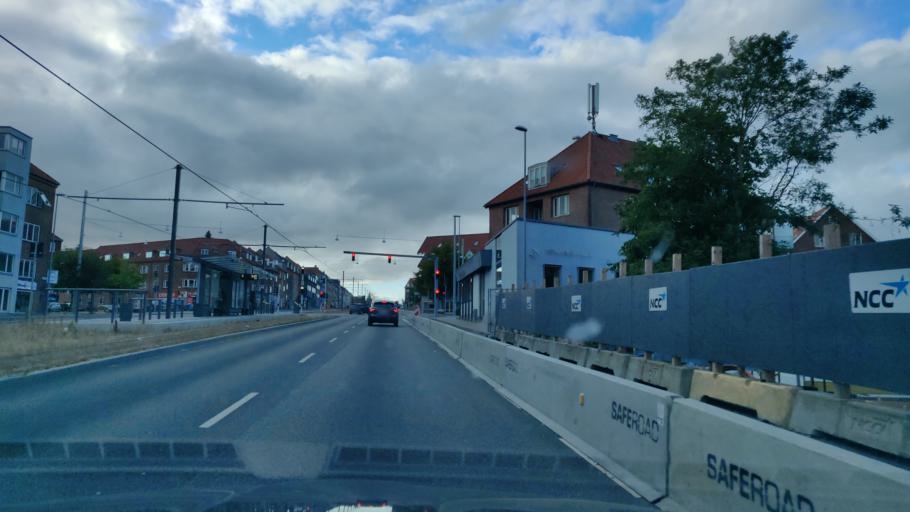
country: DK
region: Central Jutland
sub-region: Arhus Kommune
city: Arhus
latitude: 56.1735
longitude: 10.2036
